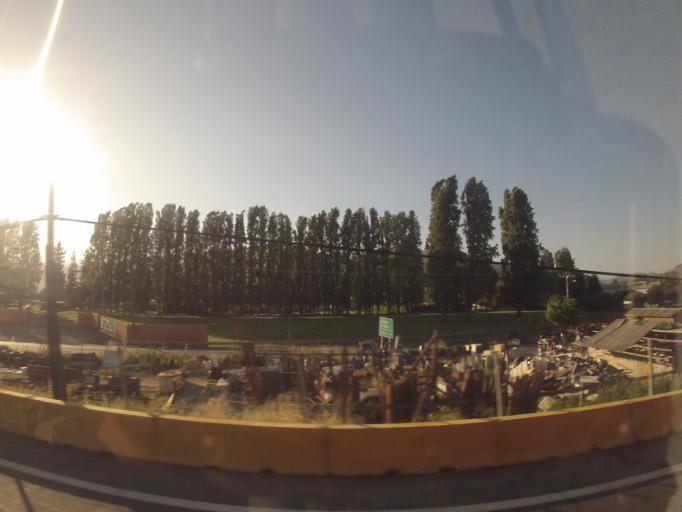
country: CL
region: O'Higgins
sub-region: Provincia de Cachapoal
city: San Vicente
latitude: -34.5533
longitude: -70.9627
